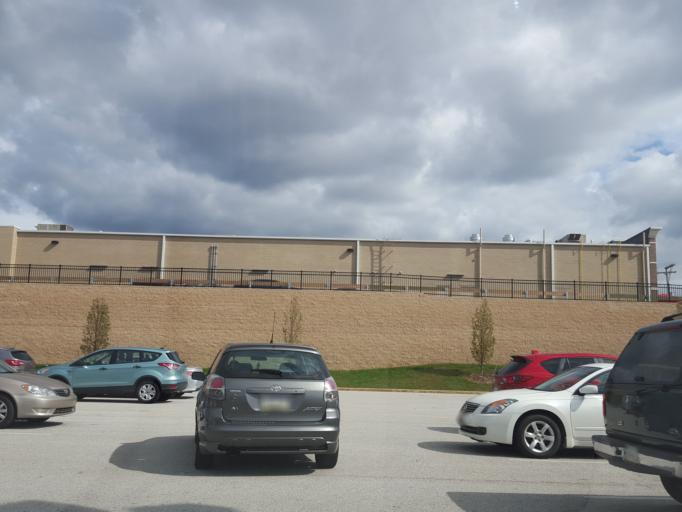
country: US
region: Pennsylvania
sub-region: York County
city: Valley View
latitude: 39.9348
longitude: -76.6927
